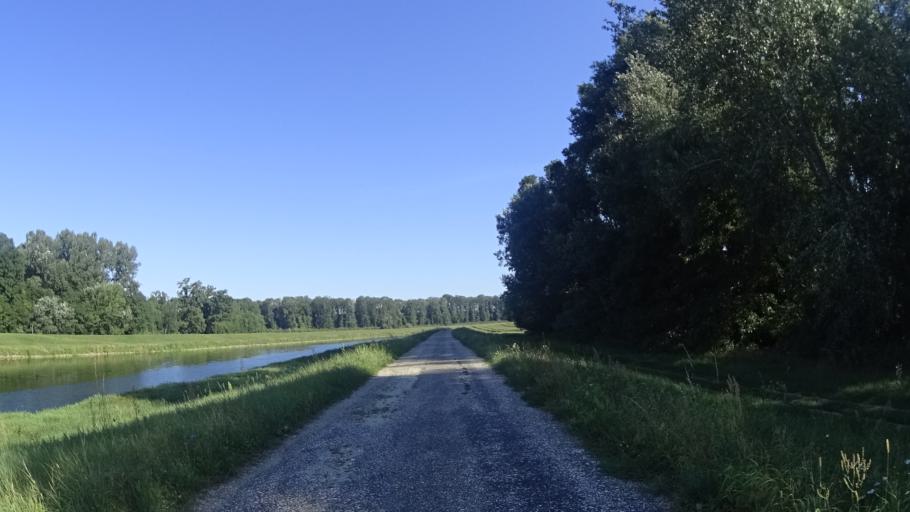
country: CZ
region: South Moravian
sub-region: Okres Breclav
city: Lanzhot
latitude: 48.7037
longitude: 16.9978
